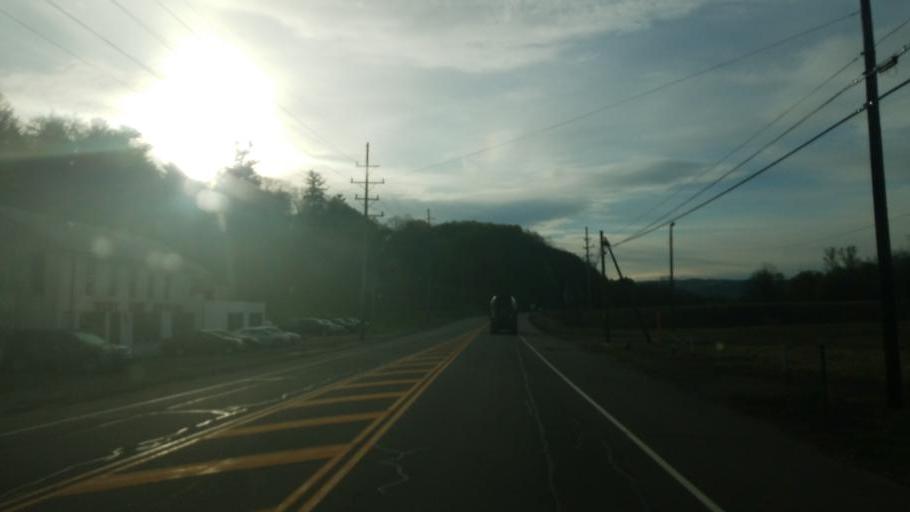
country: US
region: New York
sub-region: Steuben County
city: Hornell
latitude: 42.3339
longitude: -77.6767
